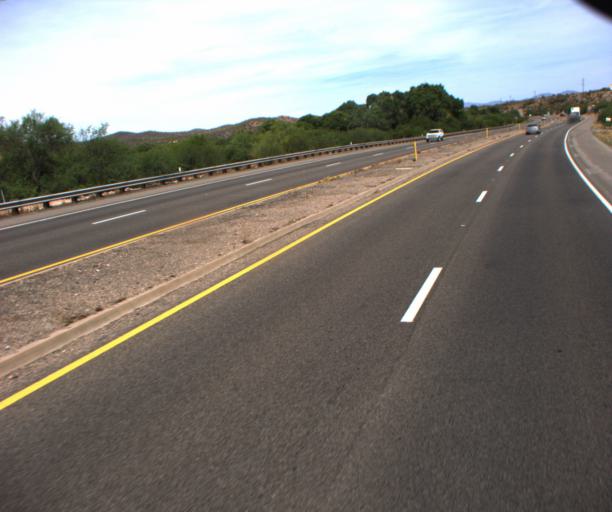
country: US
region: Arizona
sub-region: Maricopa County
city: Wickenburg
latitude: 33.8928
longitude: -112.6672
